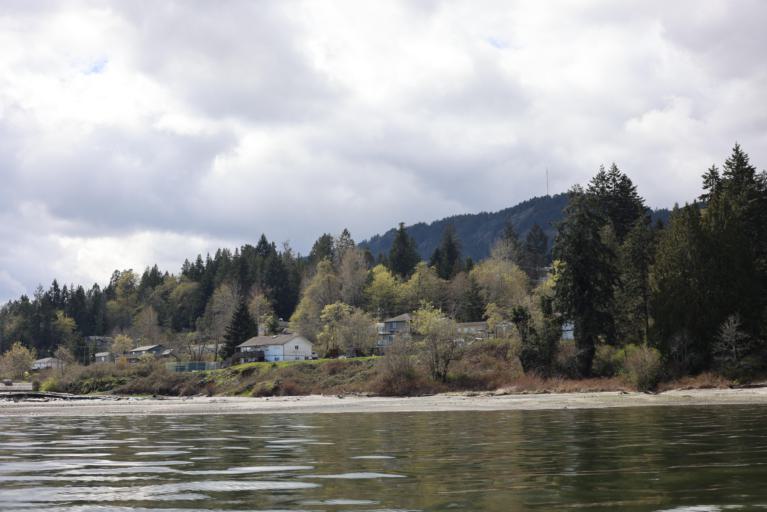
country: CA
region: British Columbia
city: North Saanich
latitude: 48.6171
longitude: -123.5182
